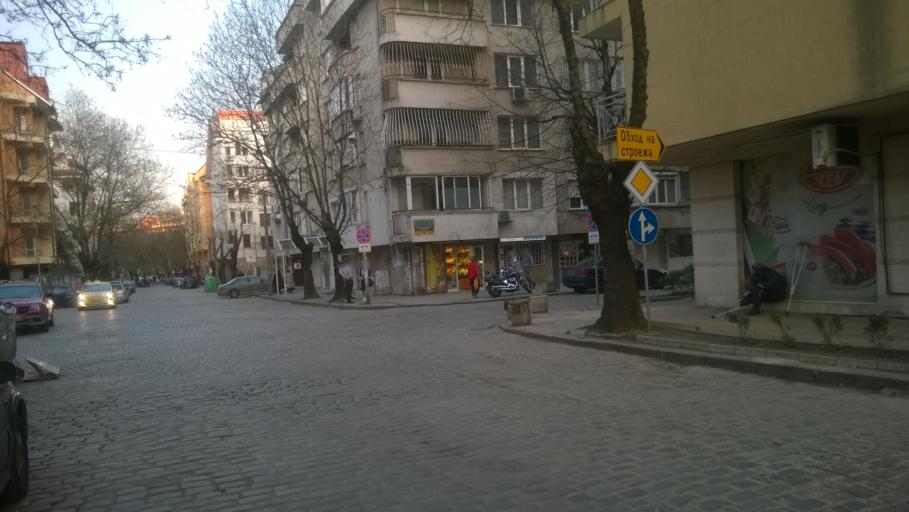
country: BG
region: Sofia-Capital
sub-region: Stolichna Obshtina
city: Sofia
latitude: 42.6804
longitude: 23.2846
